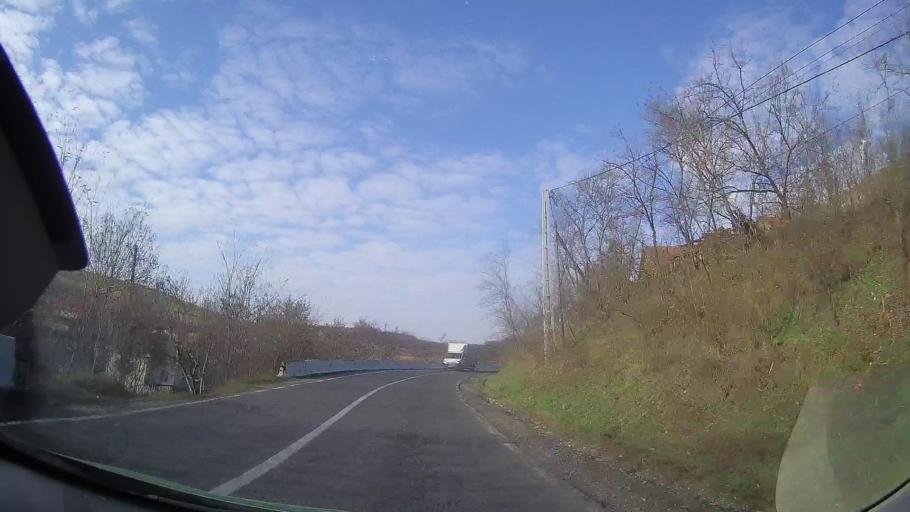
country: RO
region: Cluj
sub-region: Comuna Cojocna
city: Cojocna
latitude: 46.8051
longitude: 23.8411
